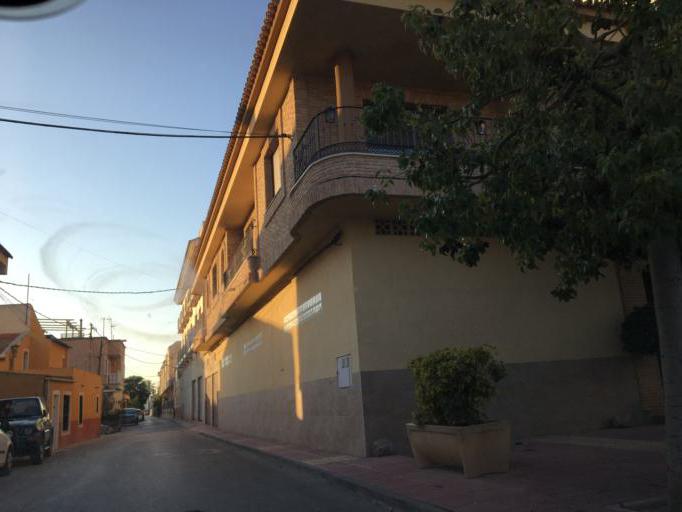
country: ES
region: Murcia
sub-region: Murcia
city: Santomera
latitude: 38.0154
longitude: -1.0533
